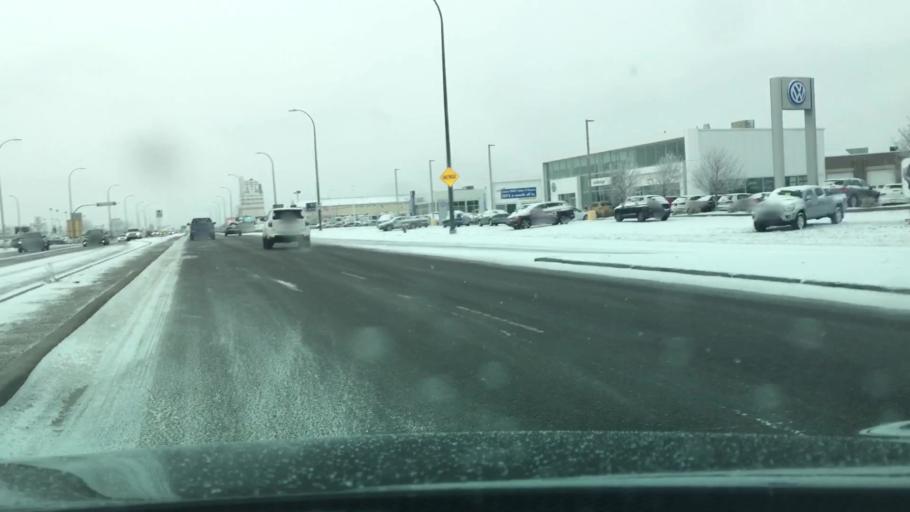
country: CA
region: Alberta
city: Lethbridge
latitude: 49.6982
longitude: -112.7880
